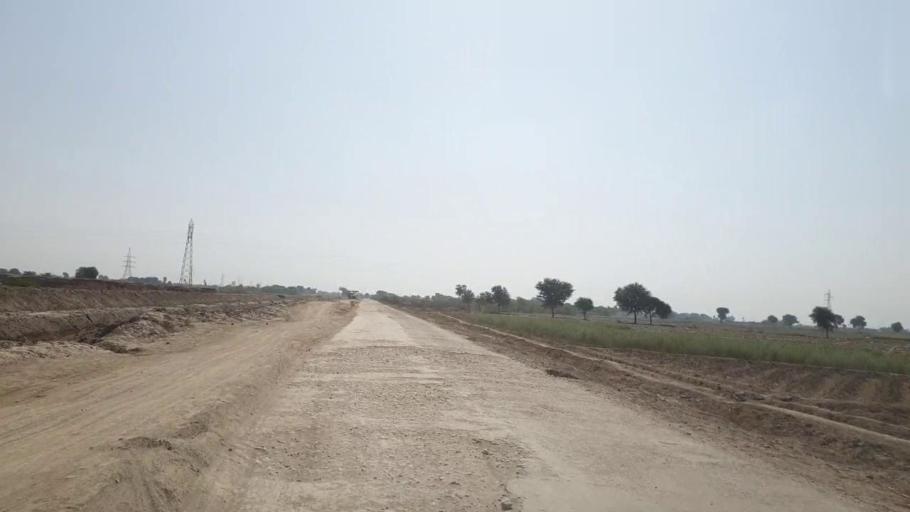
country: PK
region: Sindh
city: Naukot
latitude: 25.0067
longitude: 69.4616
